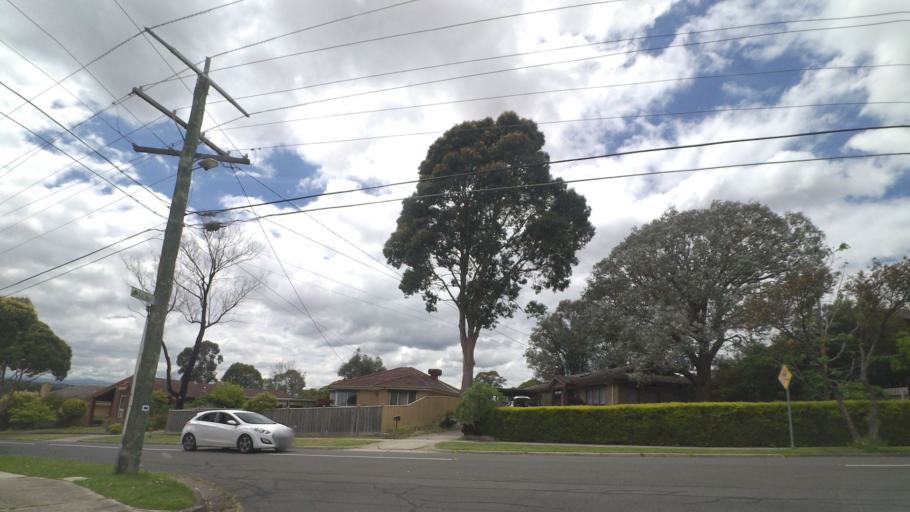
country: AU
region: Victoria
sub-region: Yarra Ranges
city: Kilsyth
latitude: -37.7982
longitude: 145.3079
